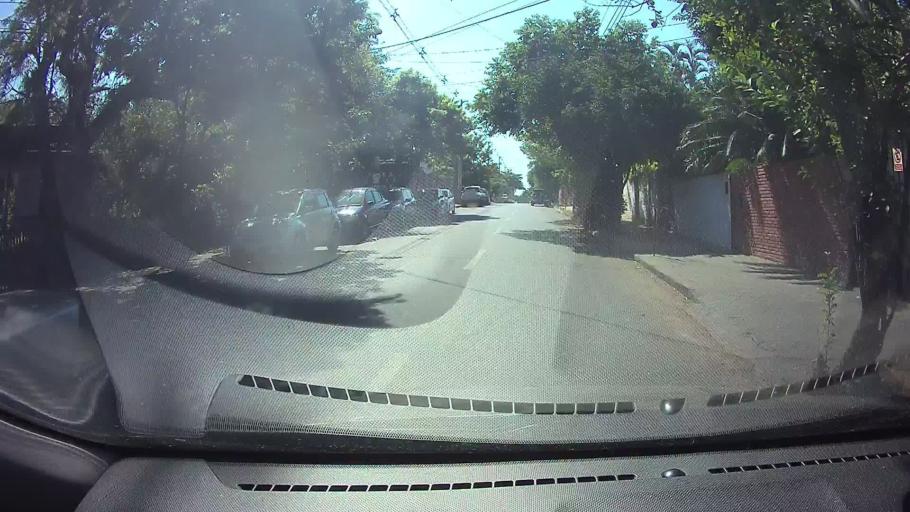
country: PY
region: Asuncion
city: Asuncion
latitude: -25.2892
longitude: -57.5707
